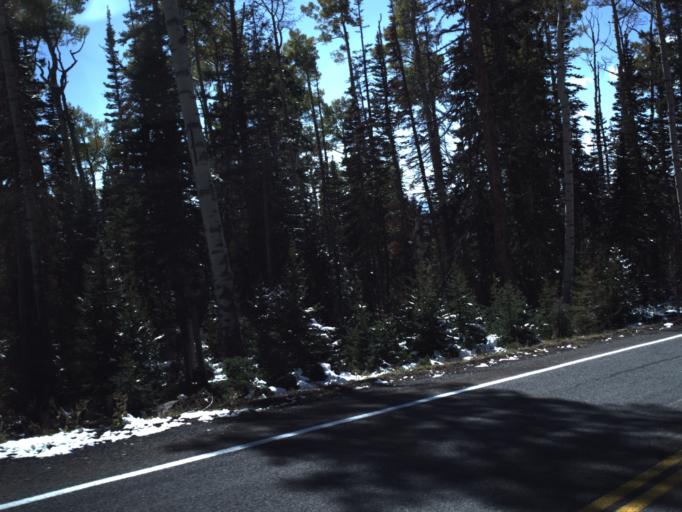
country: US
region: Utah
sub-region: Piute County
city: Junction
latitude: 38.3229
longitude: -112.3774
